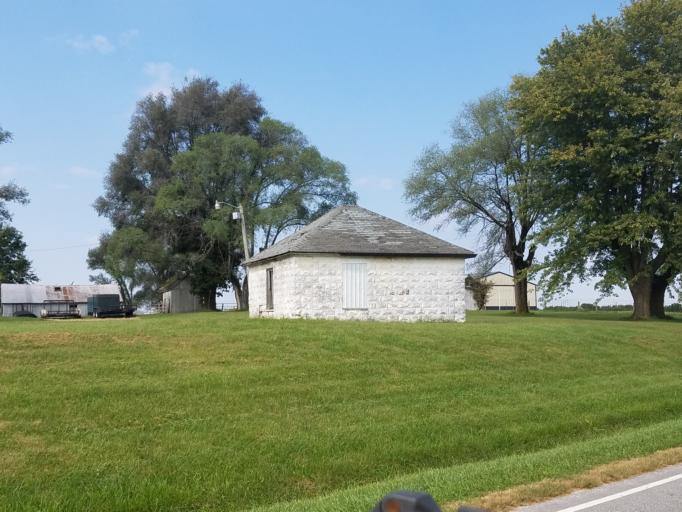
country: US
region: Missouri
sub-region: Cooper County
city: Boonville
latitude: 38.9133
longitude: -92.6830
